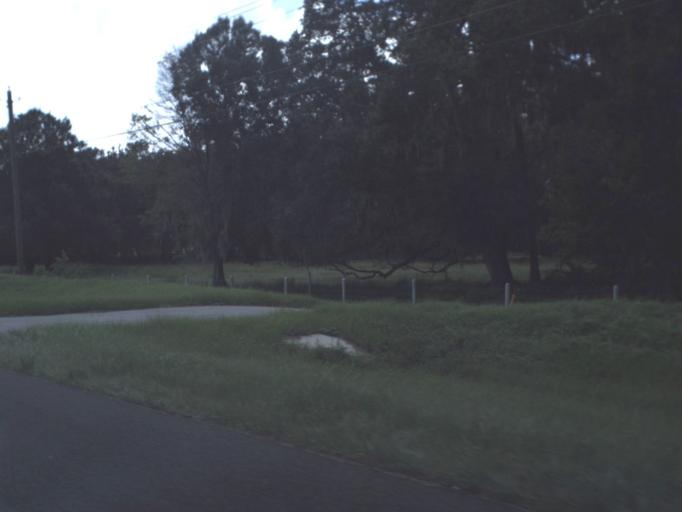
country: US
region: Florida
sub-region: Hillsborough County
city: Plant City
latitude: 28.0673
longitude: -82.1363
